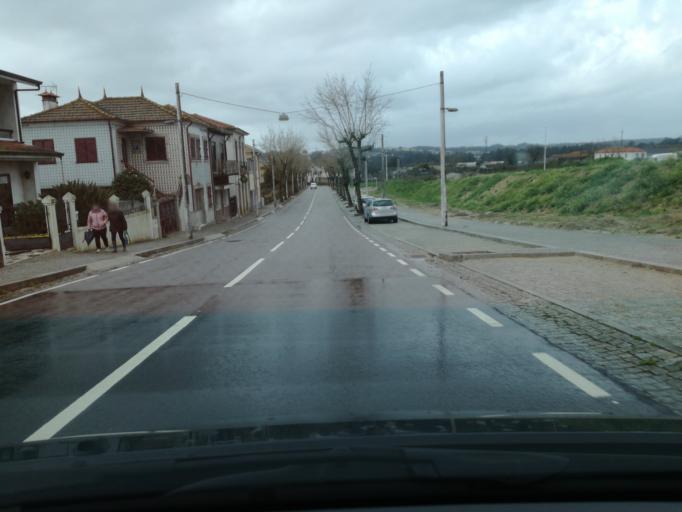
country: PT
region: Porto
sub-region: Trofa
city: Sao Romao do Coronado
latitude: 41.2597
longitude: -8.5479
